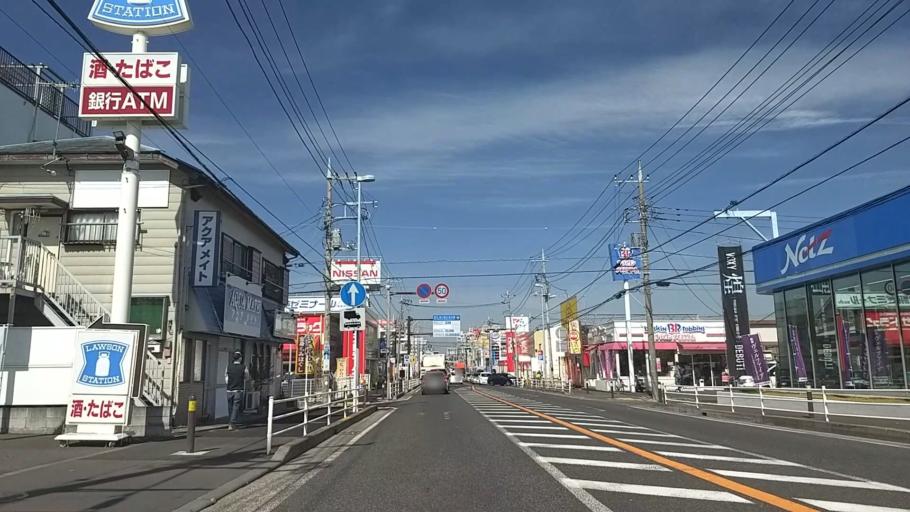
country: JP
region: Kanagawa
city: Fujisawa
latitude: 35.3925
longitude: 139.4718
